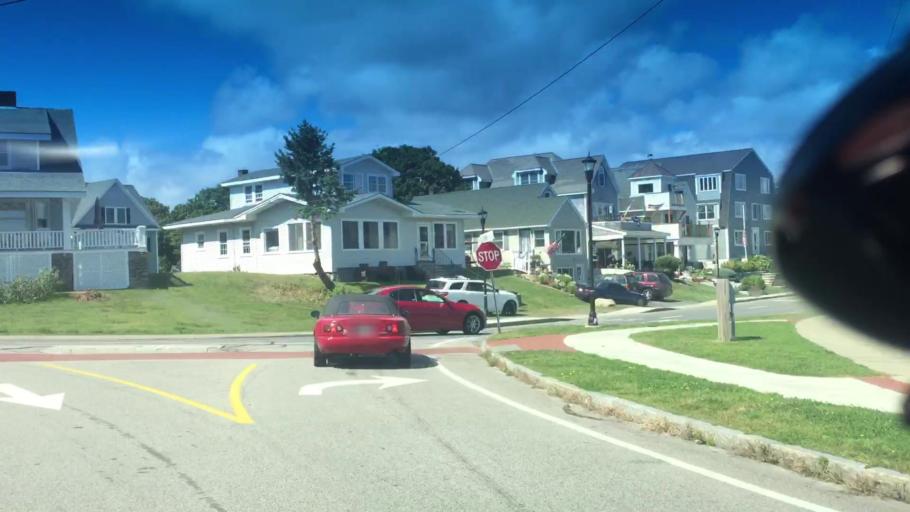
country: US
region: Maine
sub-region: York County
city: York Beach
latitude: 43.1727
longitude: -70.6068
